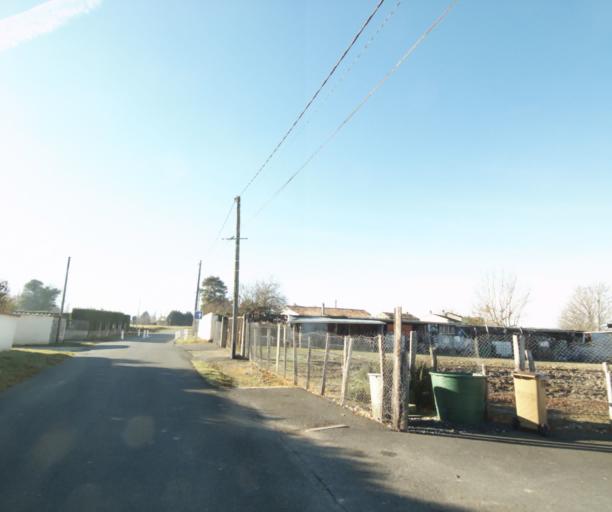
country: FR
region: Poitou-Charentes
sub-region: Departement de la Charente-Maritime
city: Fontcouverte
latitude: 45.7522
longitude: -0.5687
